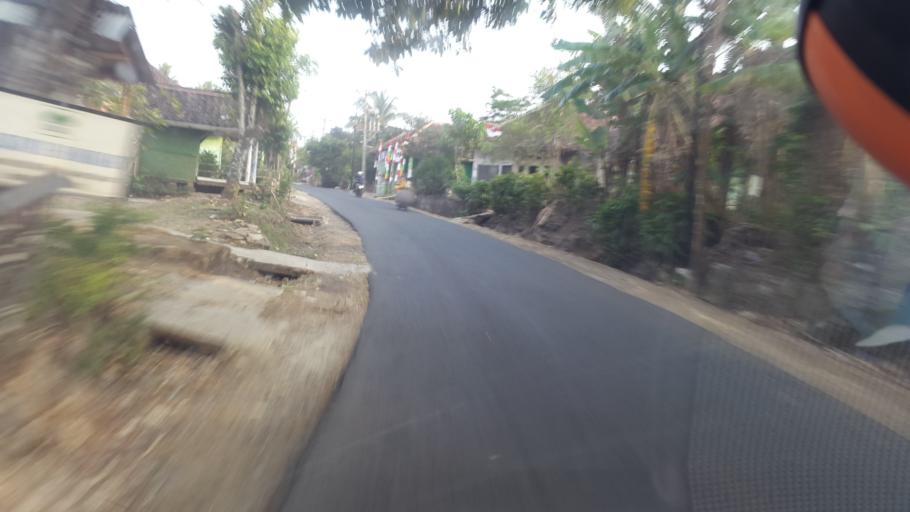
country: ID
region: West Java
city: Ciracap
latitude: -7.3444
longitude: 106.5301
